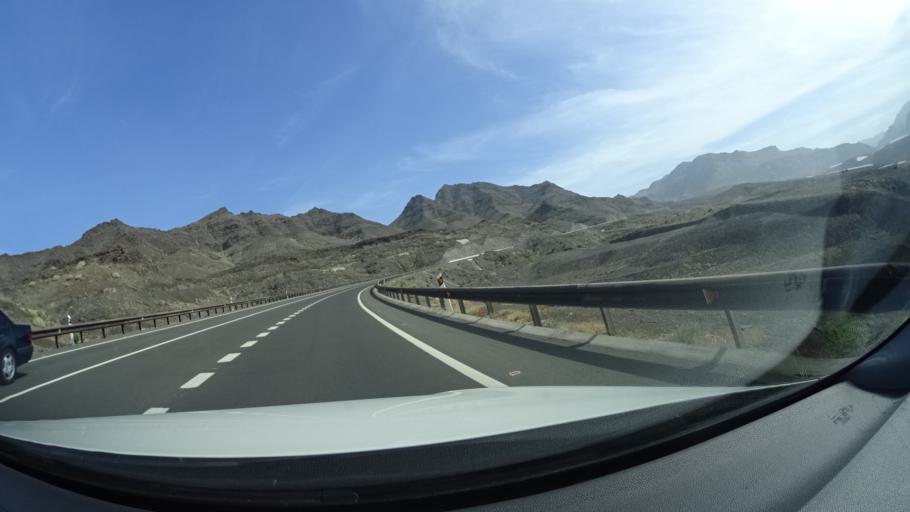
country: ES
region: Canary Islands
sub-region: Provincia de Las Palmas
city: San Nicolas
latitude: 28.0045
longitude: -15.8074
